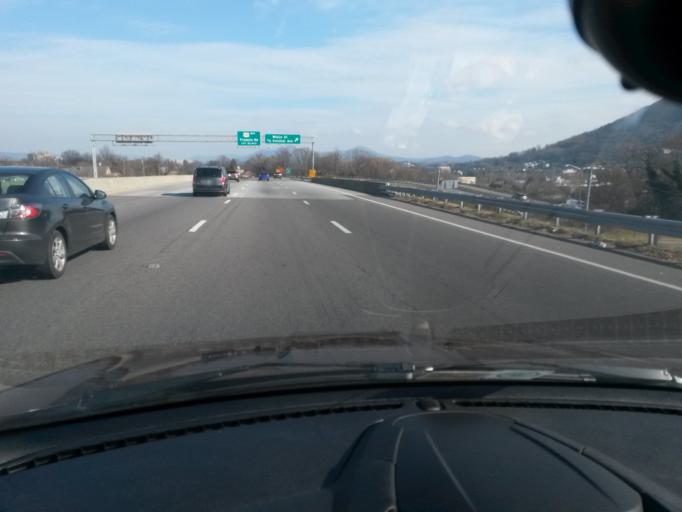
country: US
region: Virginia
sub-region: City of Roanoke
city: Roanoke
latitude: 37.2518
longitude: -79.9582
